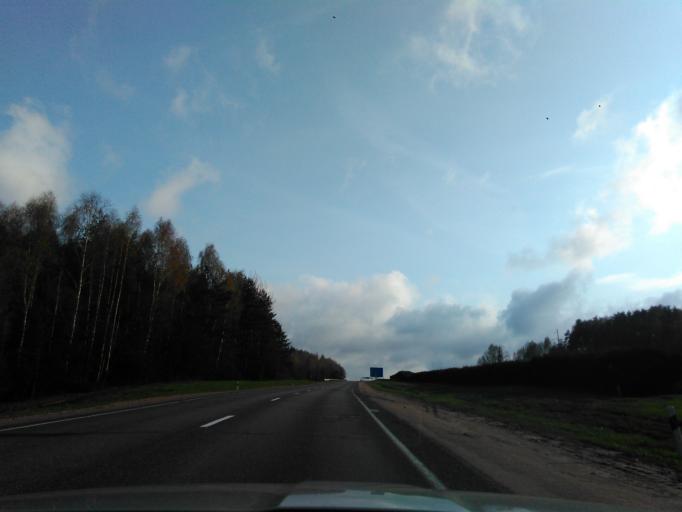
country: BY
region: Minsk
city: Lahoysk
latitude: 54.2161
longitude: 27.8300
